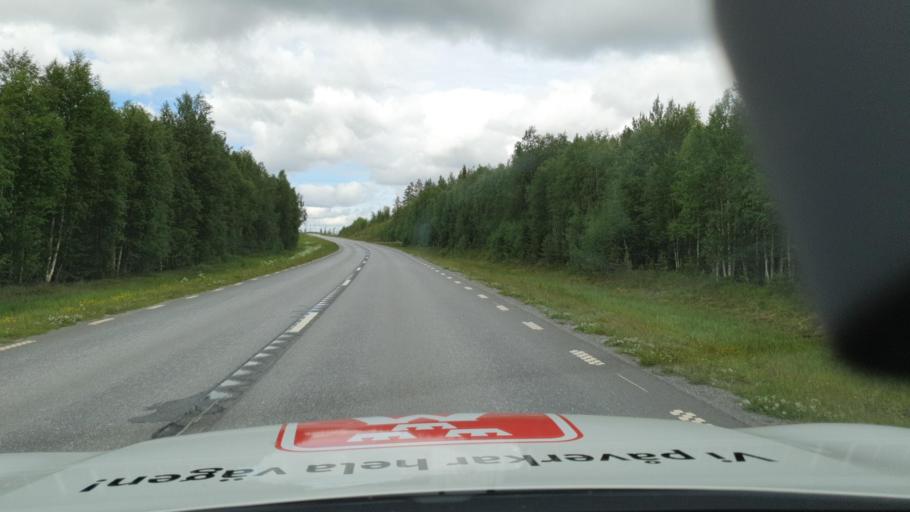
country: SE
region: Vaesterbotten
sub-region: Vilhelmina Kommun
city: Vilhelmina
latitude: 64.3985
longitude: 16.7249
